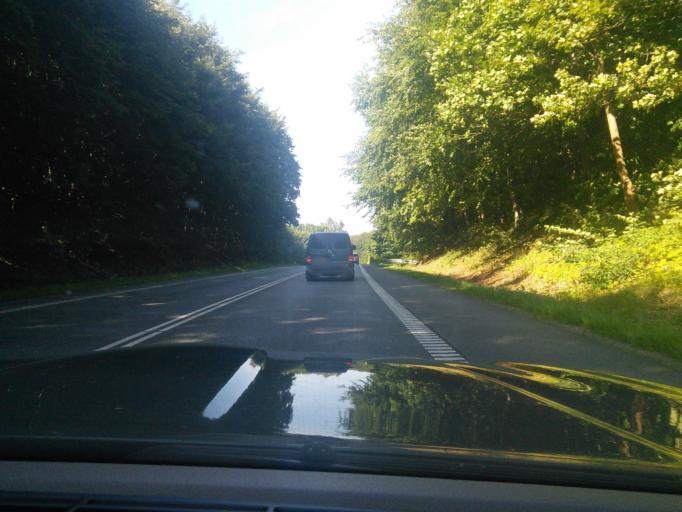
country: DK
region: Capital Region
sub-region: Halsnaes Kommune
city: Frederiksvaerk
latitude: 55.9767
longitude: 12.0290
